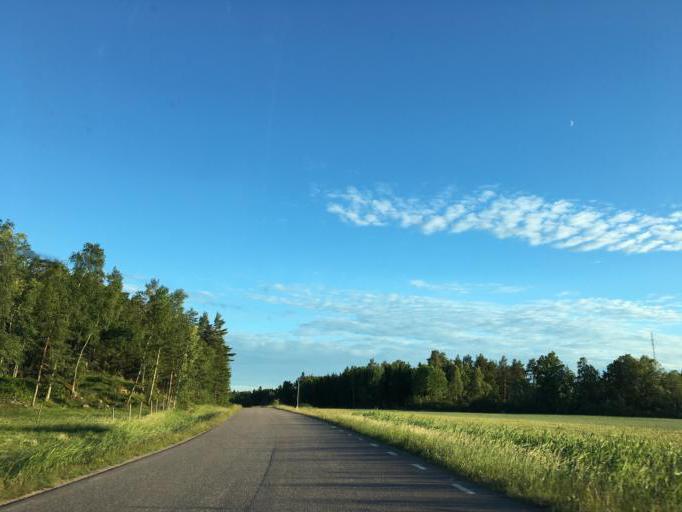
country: SE
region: Soedermanland
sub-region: Eskilstuna Kommun
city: Torshalla
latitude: 59.5225
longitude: 16.4388
